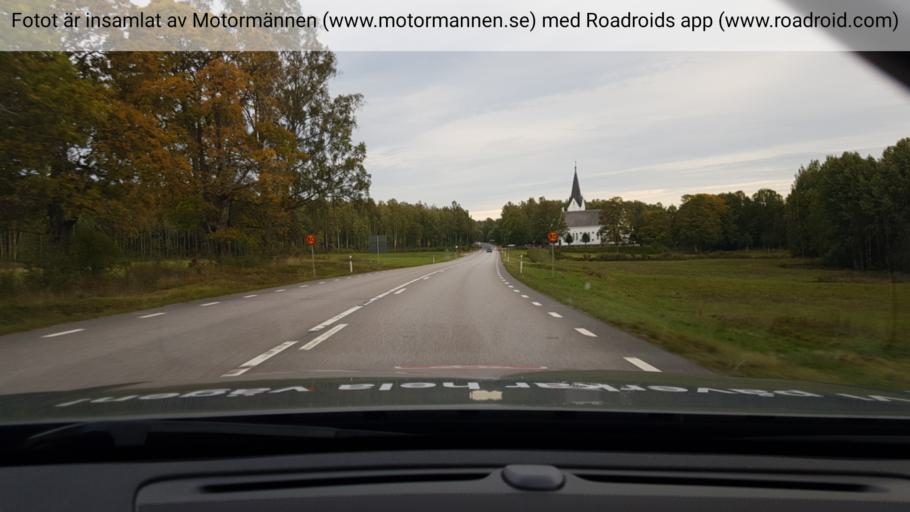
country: SE
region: Vaestra Goetaland
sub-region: Bengtsfors Kommun
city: Dals Langed
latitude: 59.0565
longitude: 12.4643
